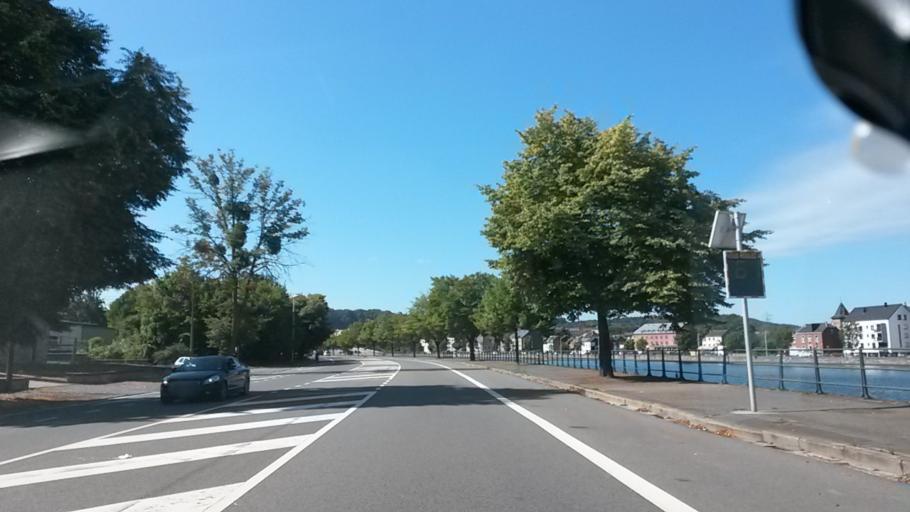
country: BE
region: Wallonia
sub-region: Province de Liege
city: Huy
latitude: 50.5313
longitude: 5.2449
